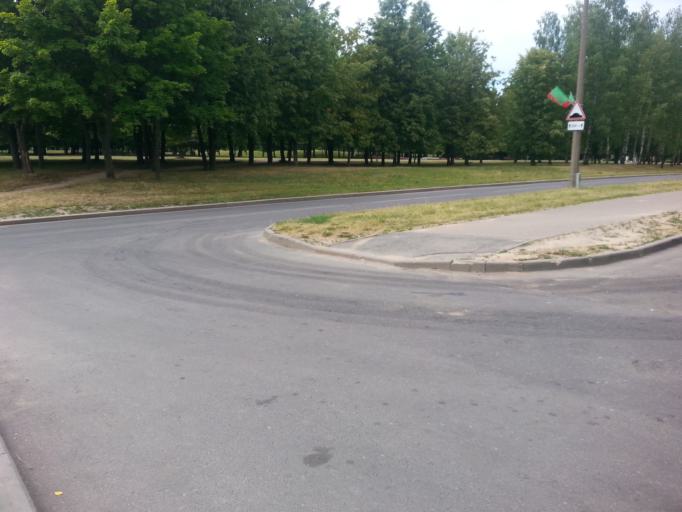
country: BY
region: Minsk
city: Novoye Medvezhino
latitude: 53.9168
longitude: 27.4877
